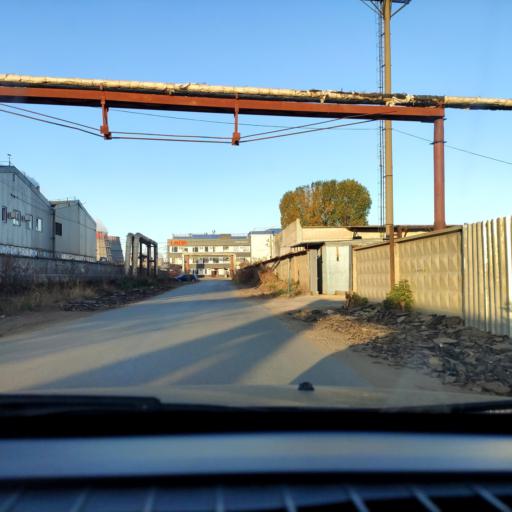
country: RU
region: Samara
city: Tol'yatti
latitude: 53.5770
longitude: 49.2651
